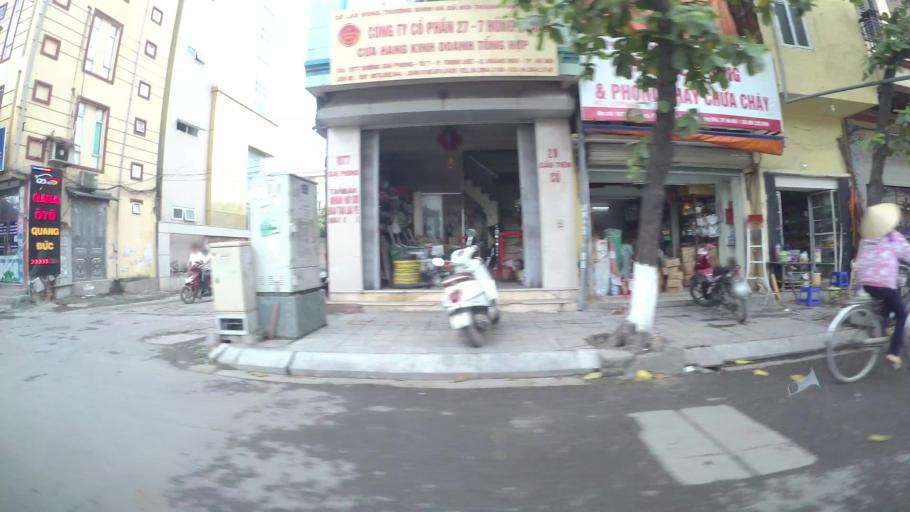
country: VN
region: Ha Noi
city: Van Dien
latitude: 20.9755
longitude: 105.8410
